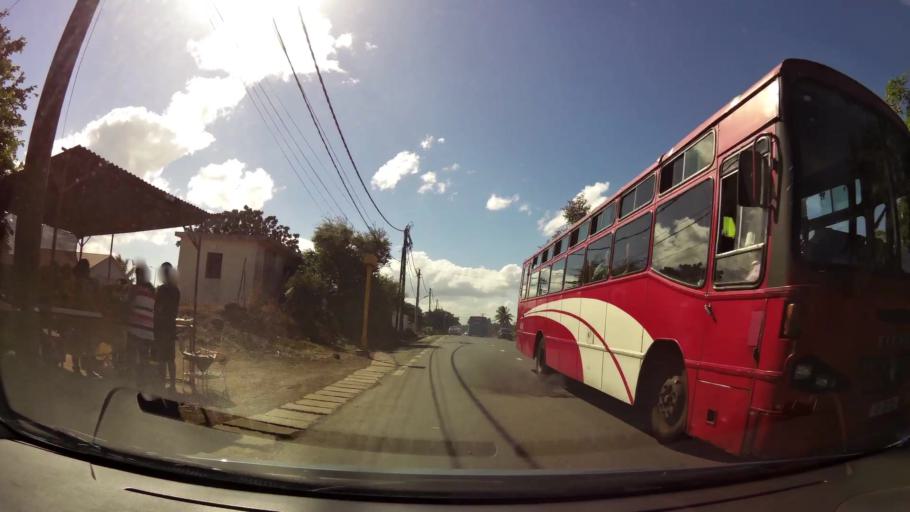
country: MU
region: Black River
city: Albion
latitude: -20.2477
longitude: 57.4208
